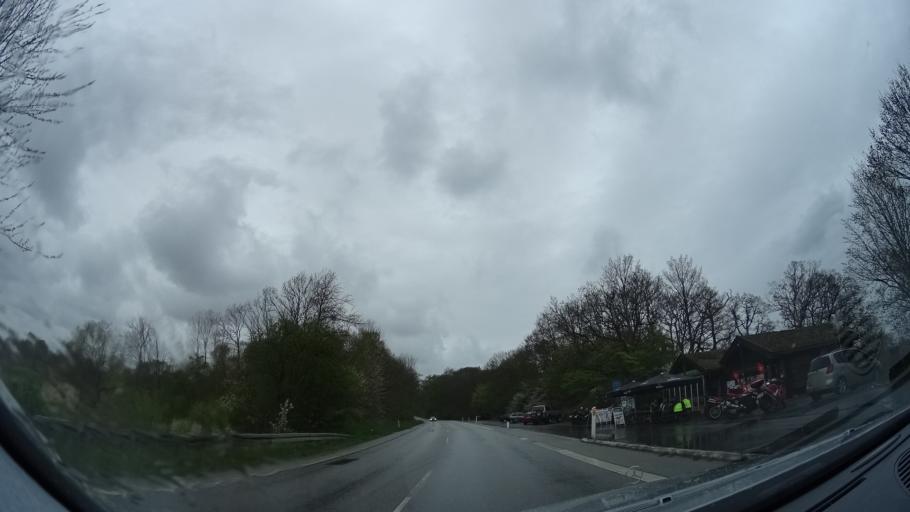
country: DK
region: Zealand
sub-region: Lejre Kommune
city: Ejby
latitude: 55.6811
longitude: 11.8034
